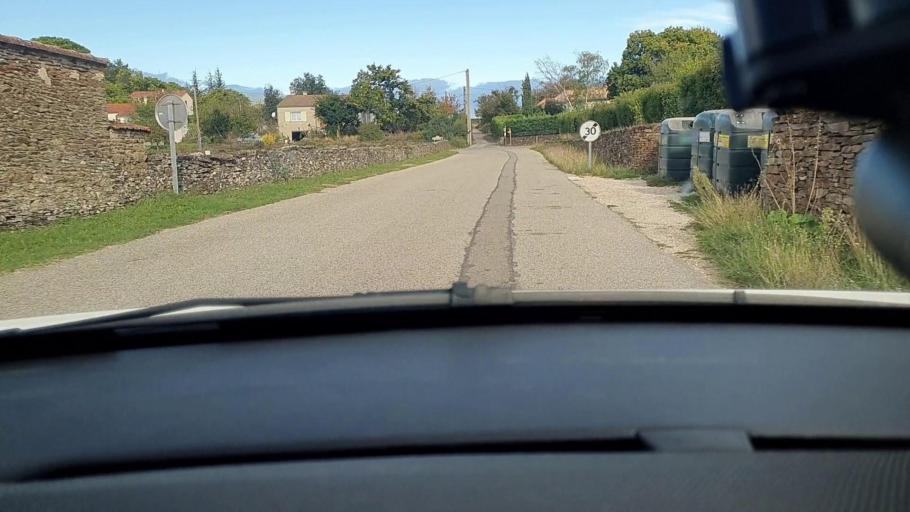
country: FR
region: Languedoc-Roussillon
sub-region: Departement du Gard
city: Besseges
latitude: 44.3261
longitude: 4.0256
